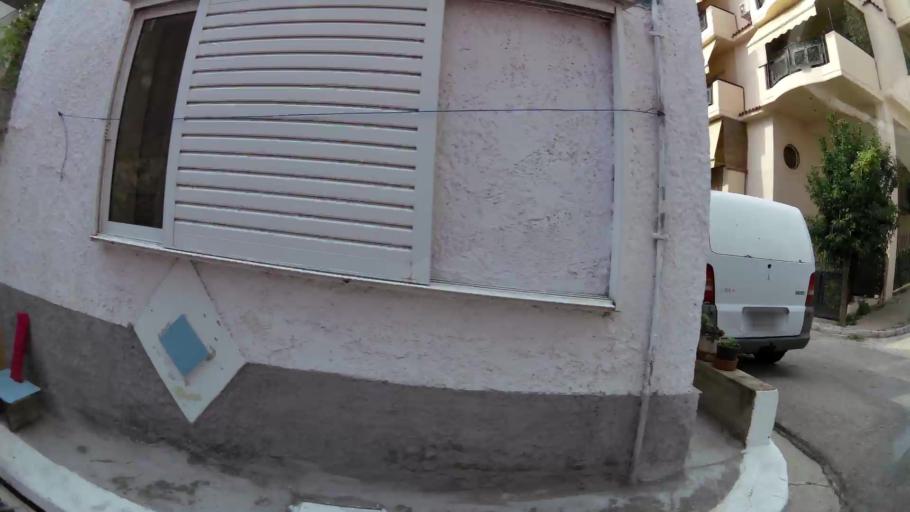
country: GR
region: Attica
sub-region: Nomarchia Athinas
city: Chaidari
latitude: 38.0232
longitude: 23.6689
